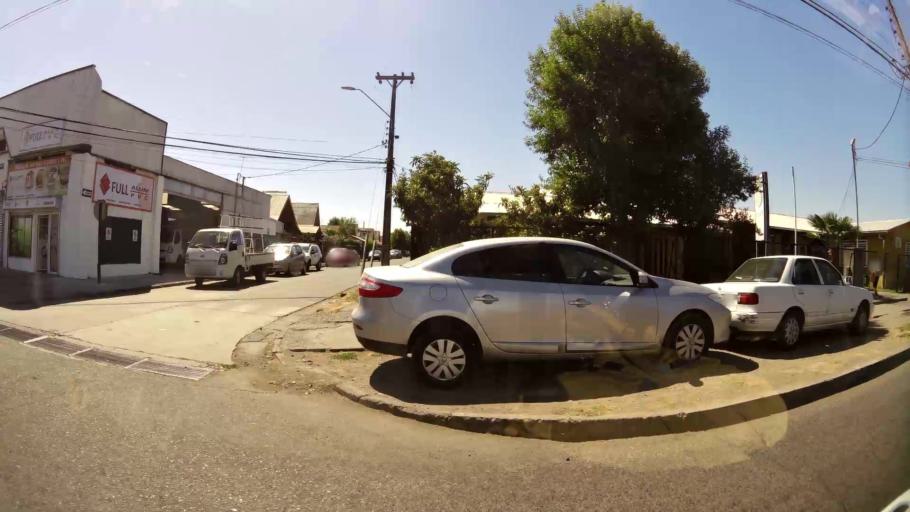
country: CL
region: Maule
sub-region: Provincia de Curico
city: Curico
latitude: -34.9726
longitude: -71.2480
